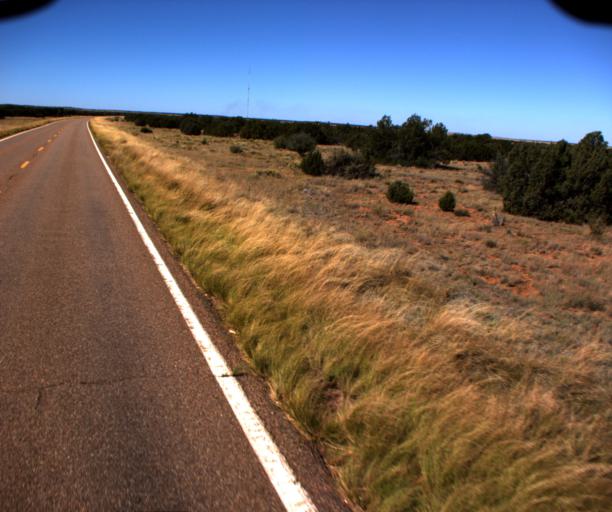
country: US
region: Arizona
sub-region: Navajo County
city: Heber-Overgaard
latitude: 34.4622
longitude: -110.3850
